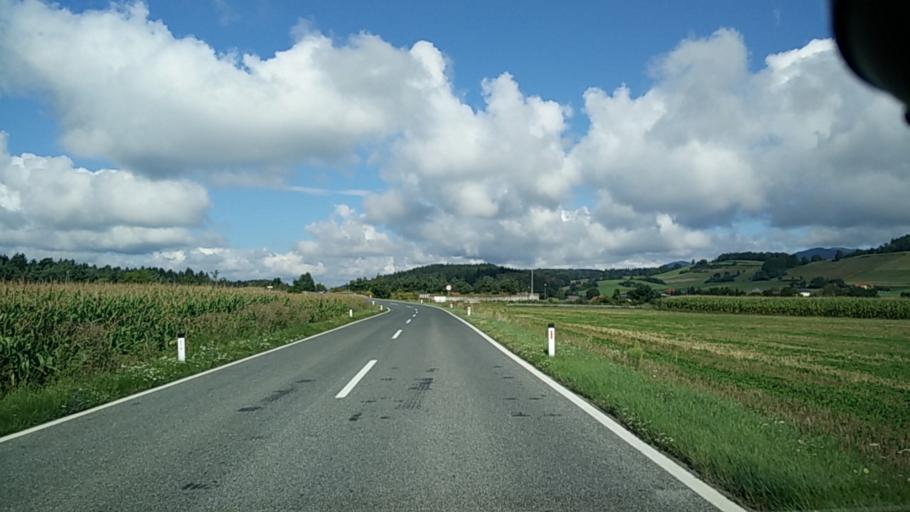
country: AT
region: Carinthia
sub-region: Politischer Bezirk Klagenfurt Land
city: Poggersdorf
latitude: 46.6465
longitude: 14.5103
